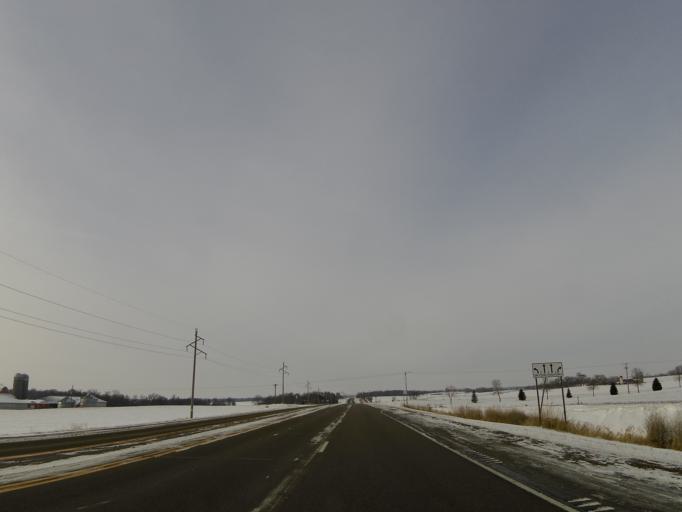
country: US
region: Minnesota
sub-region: Carver County
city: Mayer
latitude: 44.9056
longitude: -93.8362
